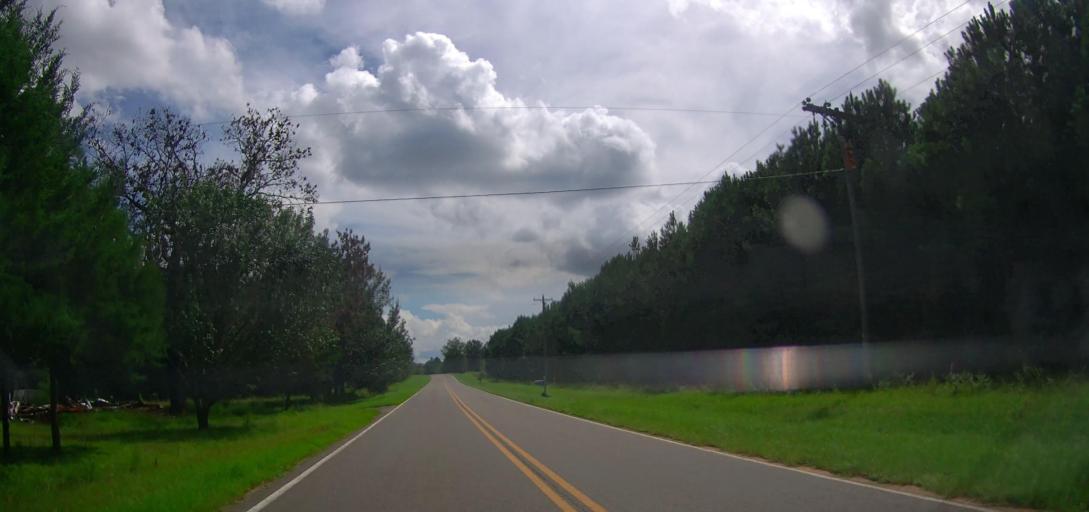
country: US
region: Georgia
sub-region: Taylor County
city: Butler
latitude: 32.4638
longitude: -84.1988
